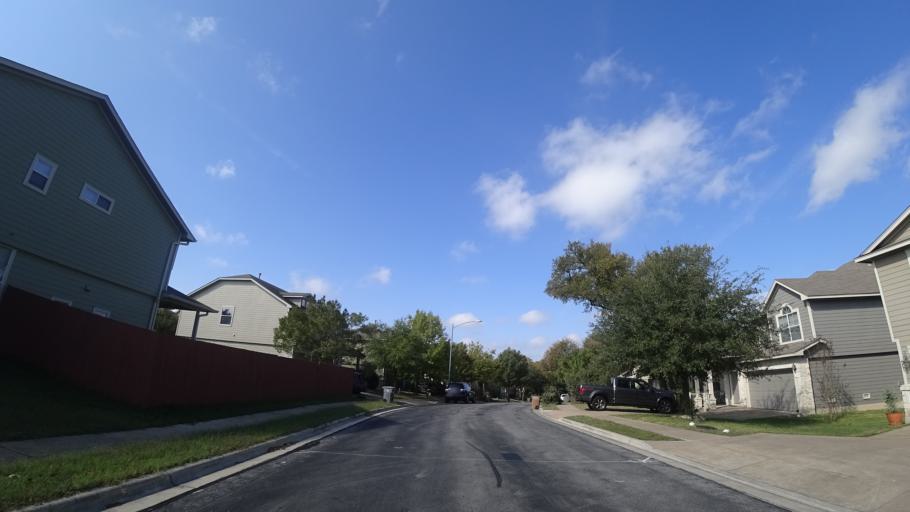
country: US
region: Texas
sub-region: Travis County
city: Shady Hollow
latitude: 30.1906
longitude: -97.8190
